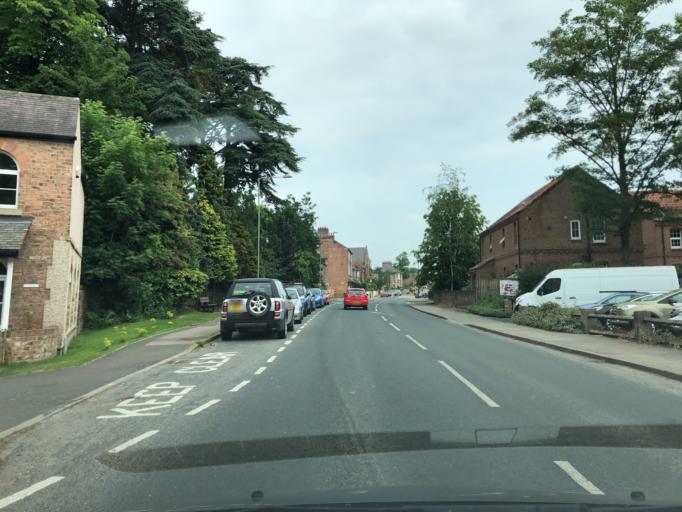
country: GB
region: England
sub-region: North Yorkshire
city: Boroughbridge
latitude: 54.0926
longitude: -1.3982
